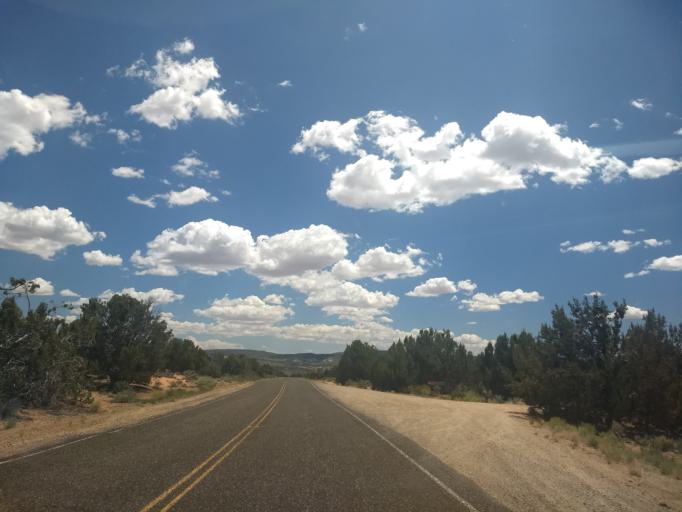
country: US
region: Utah
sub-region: Kane County
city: Kanab
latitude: 37.1848
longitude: -112.6542
